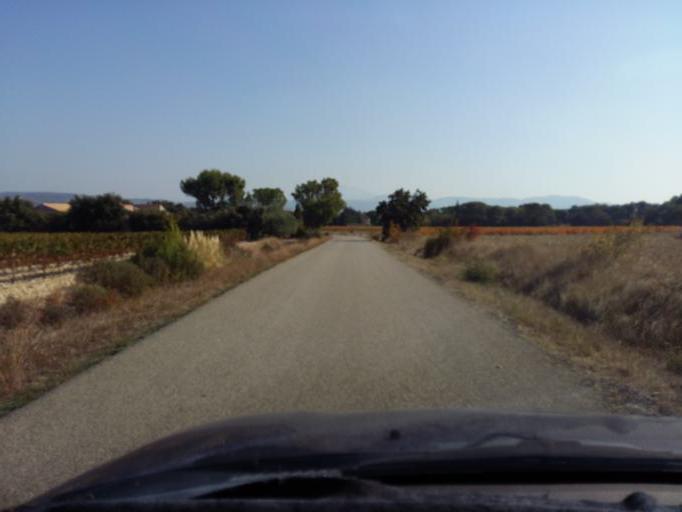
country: FR
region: Provence-Alpes-Cote d'Azur
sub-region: Departement du Vaucluse
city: Sainte-Cecile-les-Vignes
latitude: 44.2263
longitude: 4.8593
